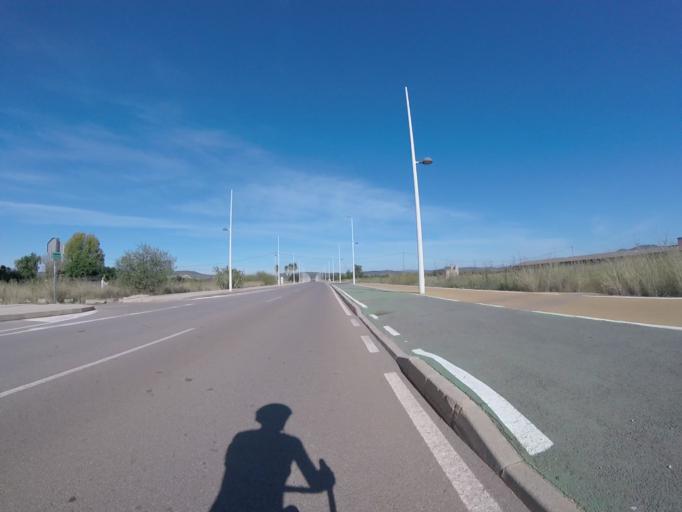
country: ES
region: Valencia
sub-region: Provincia de Castello
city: Torreblanca
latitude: 40.2118
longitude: 0.2238
